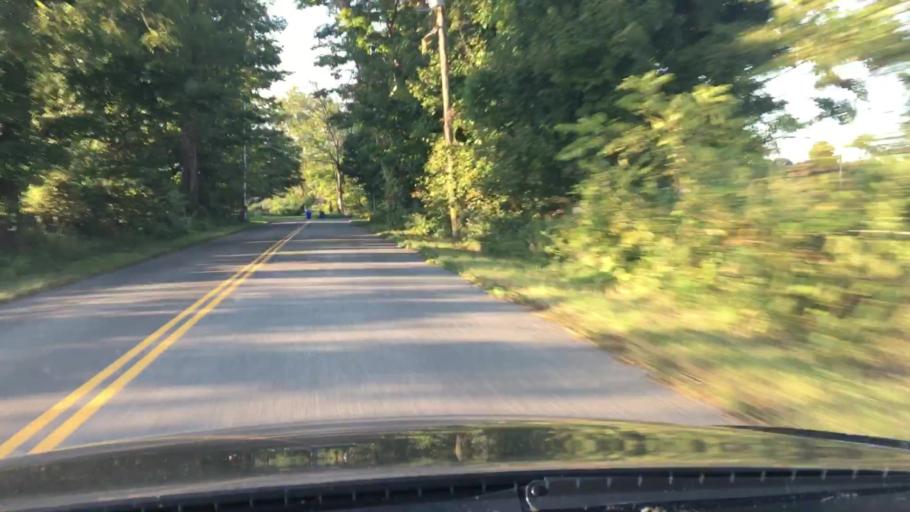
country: US
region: Connecticut
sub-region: Litchfield County
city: New Milford
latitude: 41.5998
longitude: -73.3739
